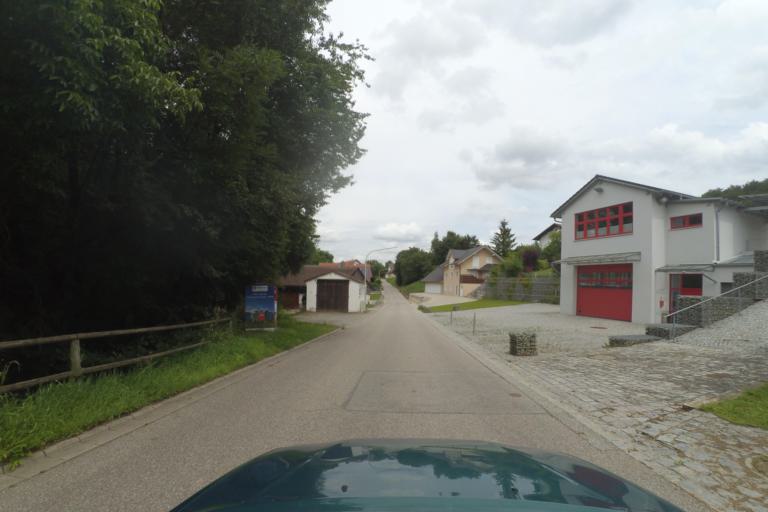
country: DE
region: Bavaria
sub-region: Lower Bavaria
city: Mamming
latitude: 48.6611
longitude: 12.6455
